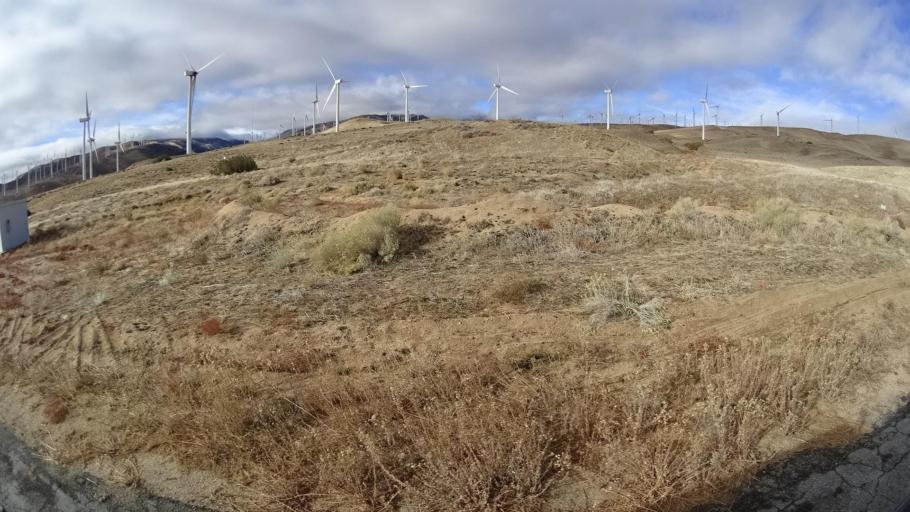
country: US
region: California
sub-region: Kern County
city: Tehachapi
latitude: 35.0603
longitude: -118.3534
